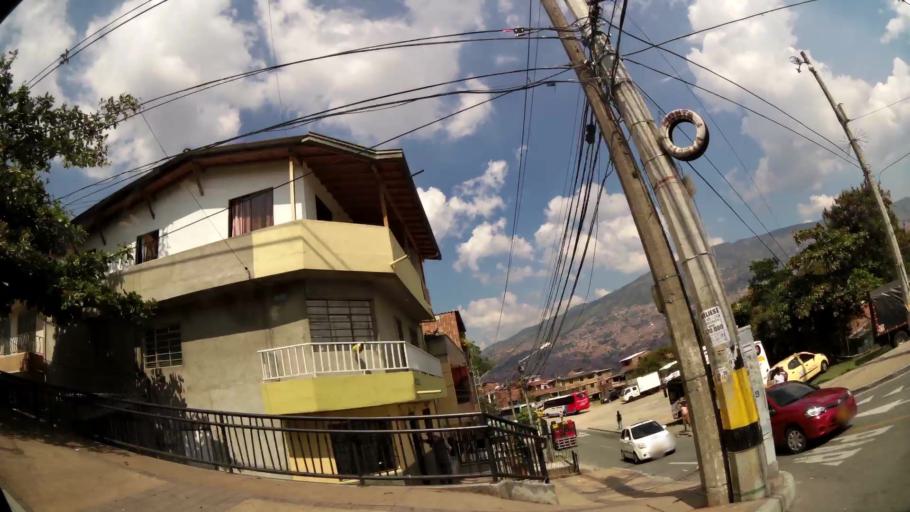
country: CO
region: Antioquia
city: Medellin
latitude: 6.2865
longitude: -75.5778
